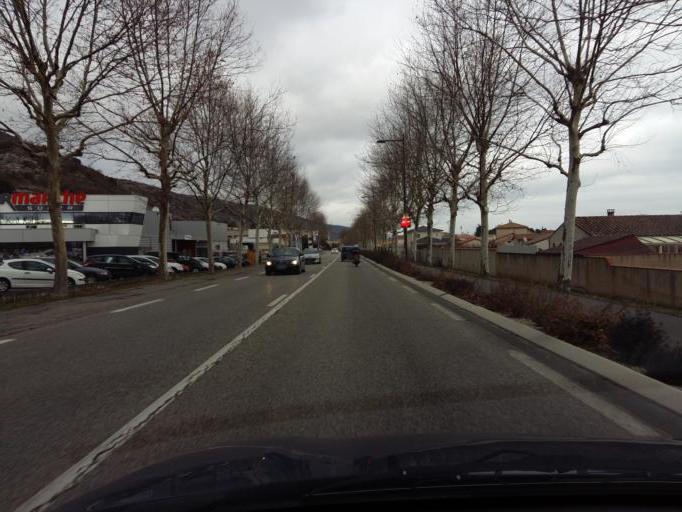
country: FR
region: Rhone-Alpes
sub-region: Departement de l'Ardeche
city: Le Pouzin
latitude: 44.7447
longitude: 4.7445
